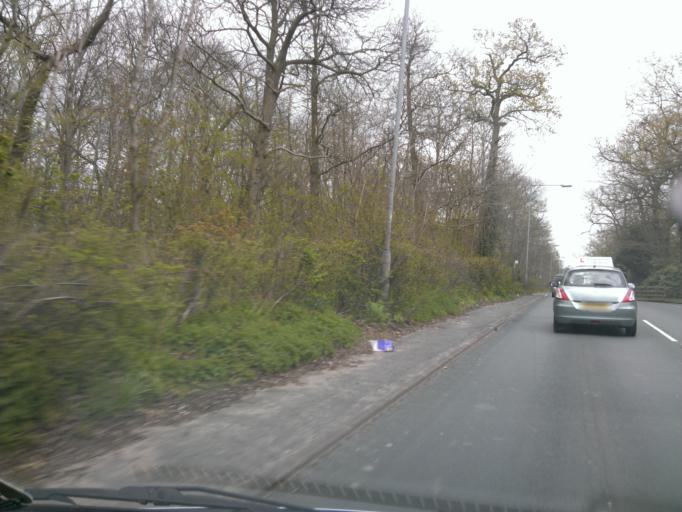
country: GB
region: England
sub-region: Essex
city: Rowhedge
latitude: 51.8795
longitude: 0.9544
